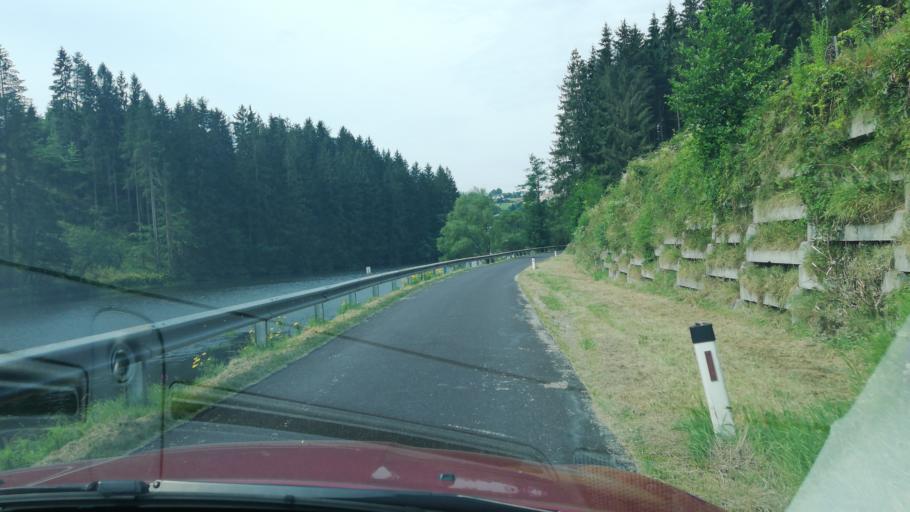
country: AT
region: Upper Austria
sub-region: Politischer Bezirk Rohrbach
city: Kleinzell im Muehlkreis
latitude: 48.4914
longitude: 14.0048
